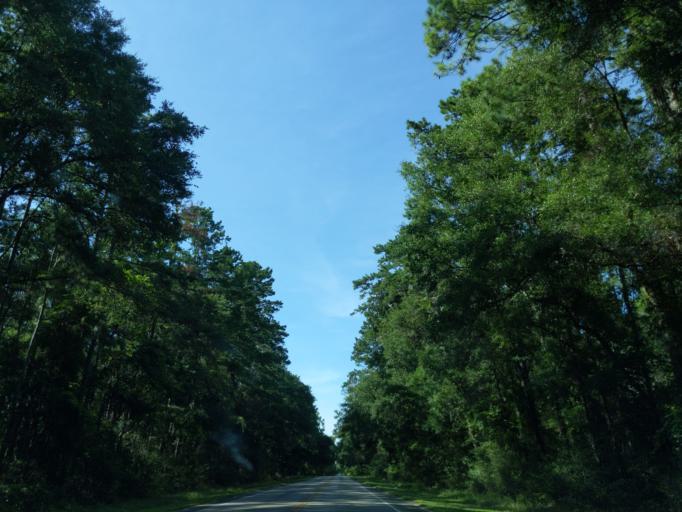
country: US
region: Florida
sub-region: Leon County
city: Woodville
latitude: 30.2713
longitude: -84.3126
